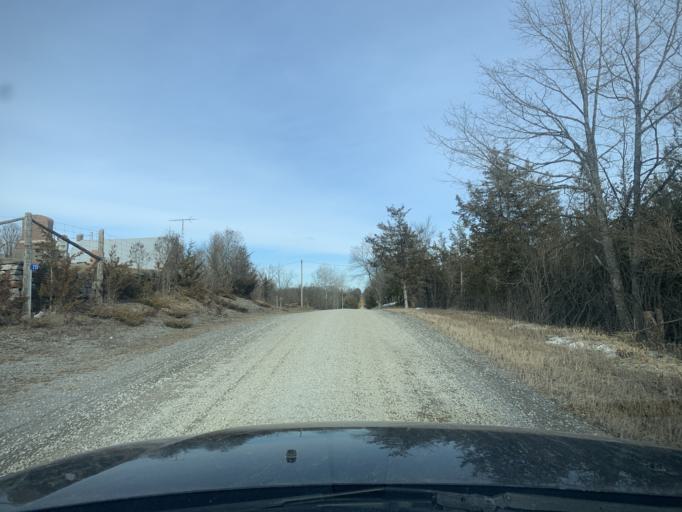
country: CA
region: Ontario
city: Deseronto
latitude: 44.3968
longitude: -77.1463
